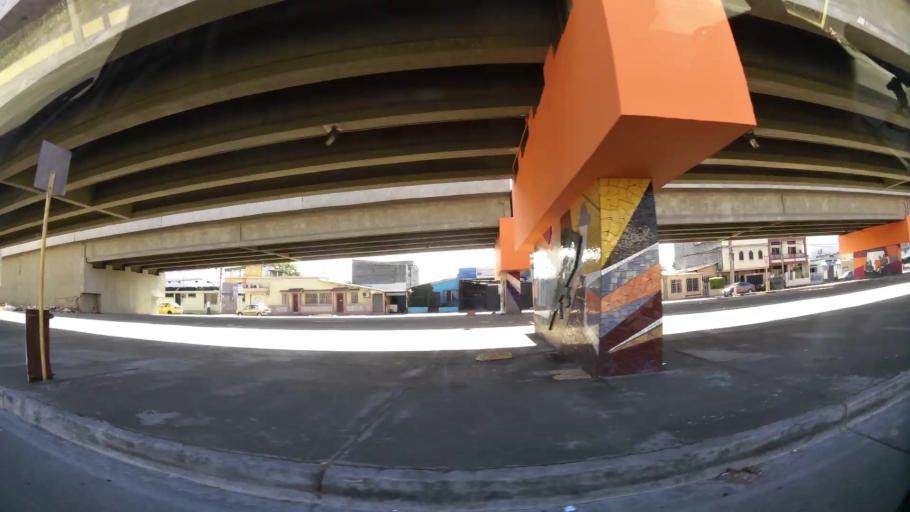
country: EC
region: Guayas
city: Eloy Alfaro
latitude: -2.1464
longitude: -79.9004
